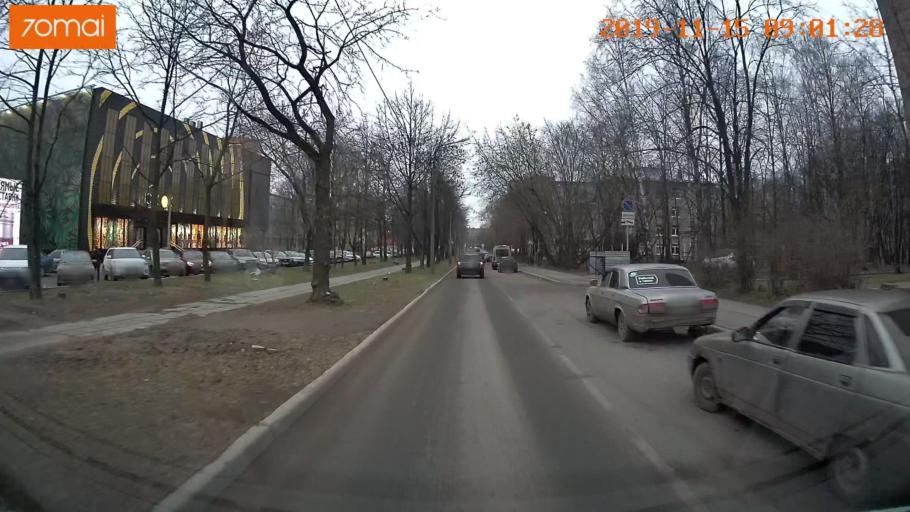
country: RU
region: Vologda
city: Cherepovets
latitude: 59.1324
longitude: 37.9259
